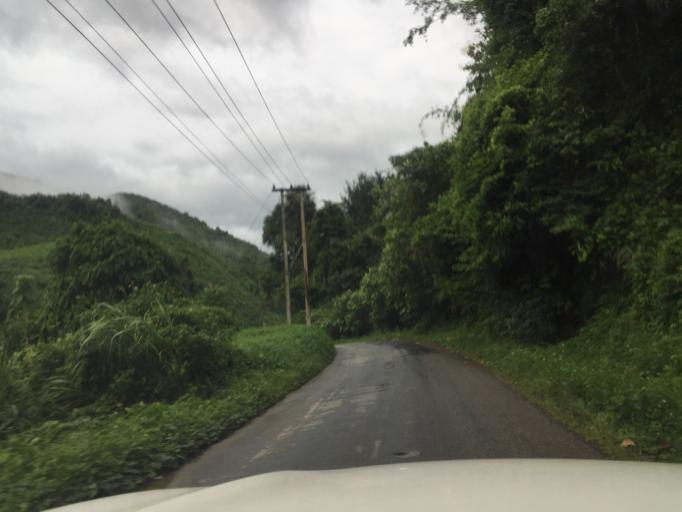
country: LA
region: Oudomxai
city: Muang La
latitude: 21.0306
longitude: 102.2367
